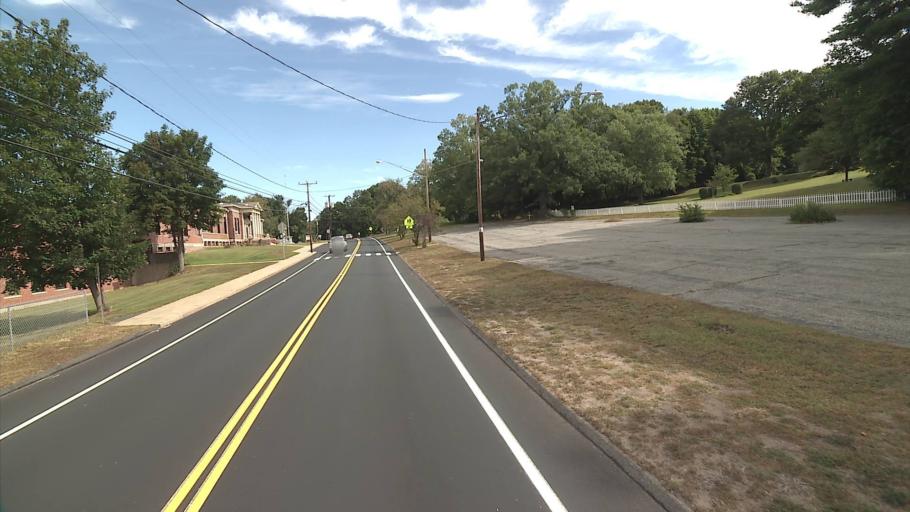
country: US
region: Connecticut
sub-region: Tolland County
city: Storrs
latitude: 41.8507
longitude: -72.3021
